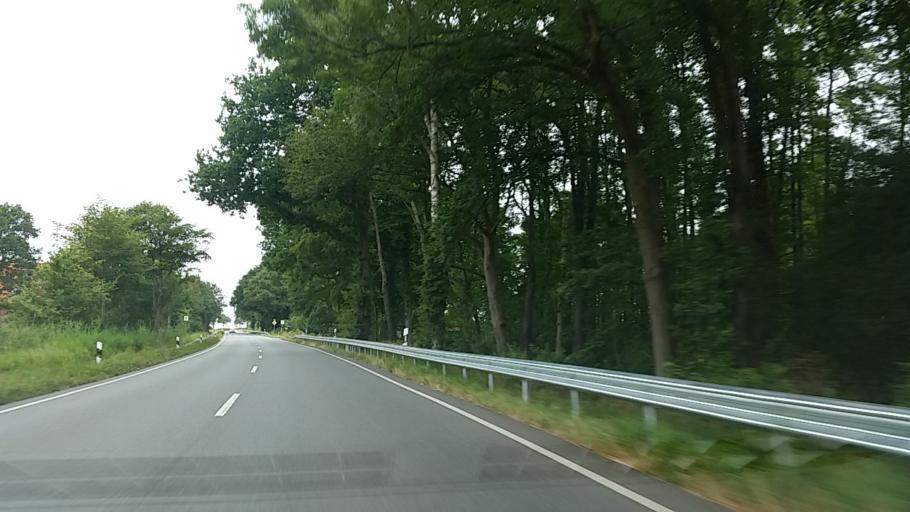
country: DE
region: Lower Saxony
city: Beverstedt
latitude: 53.4270
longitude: 8.8856
